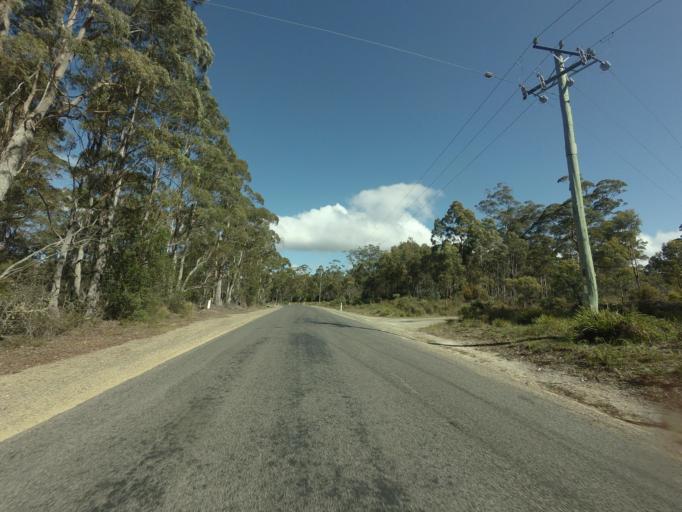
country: AU
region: Tasmania
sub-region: Break O'Day
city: St Helens
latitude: -41.6147
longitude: 148.2140
